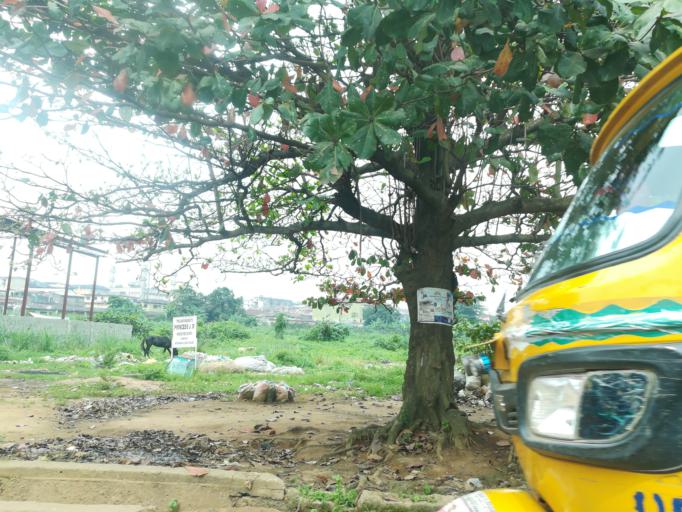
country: NG
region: Lagos
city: Ikorodu
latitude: 6.6224
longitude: 3.5069
